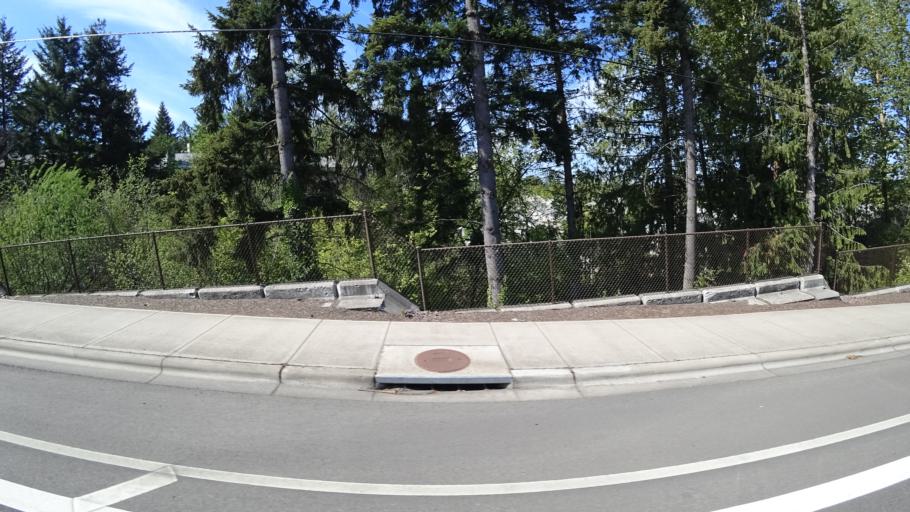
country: US
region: Oregon
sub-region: Washington County
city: King City
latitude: 45.4343
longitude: -122.8338
